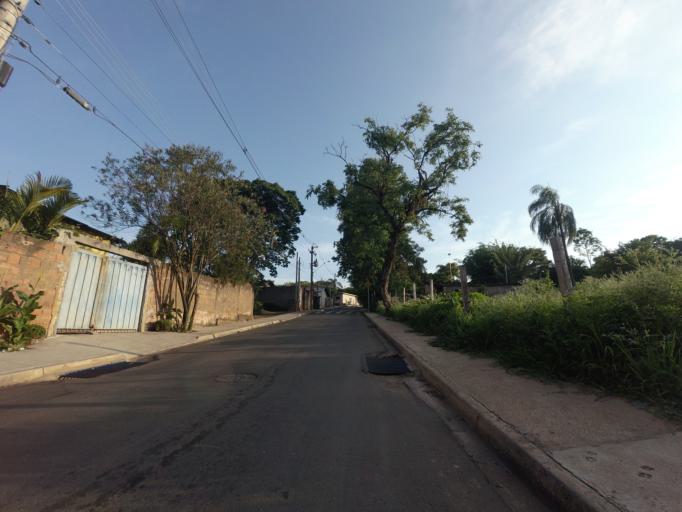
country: BR
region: Sao Paulo
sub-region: Piracicaba
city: Piracicaba
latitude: -22.7493
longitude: -47.6100
